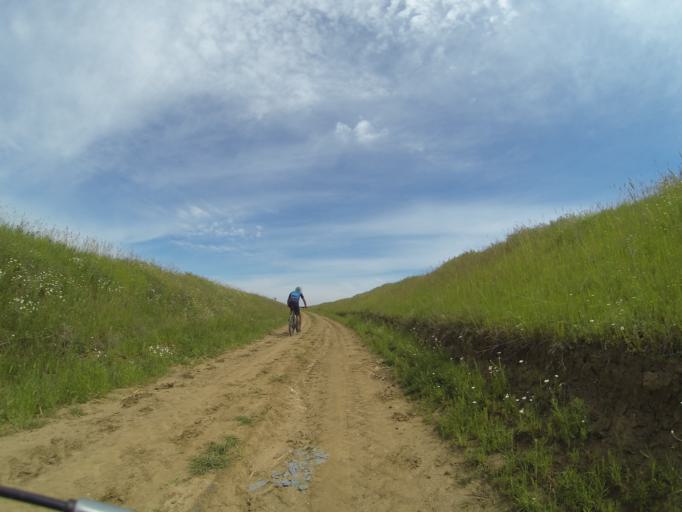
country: RO
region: Dolj
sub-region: Comuna Leu
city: Leu
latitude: 44.2011
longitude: 23.9930
